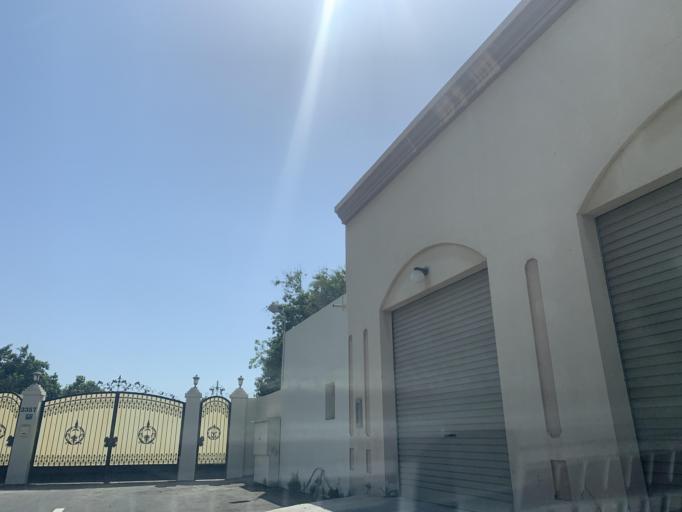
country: BH
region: Manama
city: Jidd Hafs
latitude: 26.2294
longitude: 50.5022
